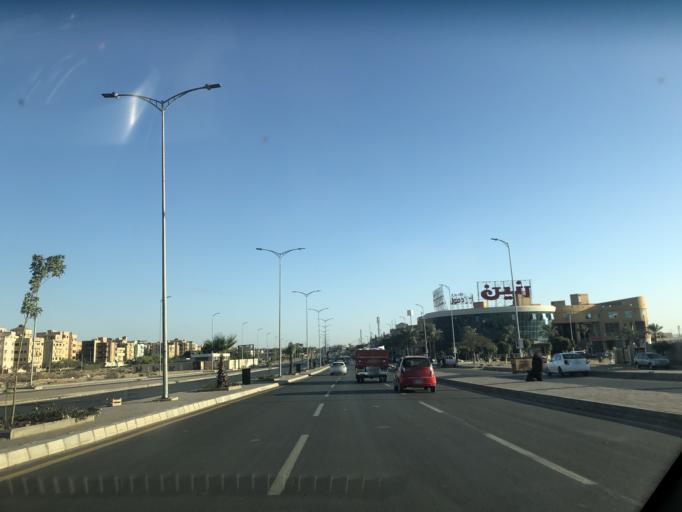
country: EG
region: Al Jizah
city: Madinat Sittah Uktubar
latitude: 29.9499
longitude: 30.9128
